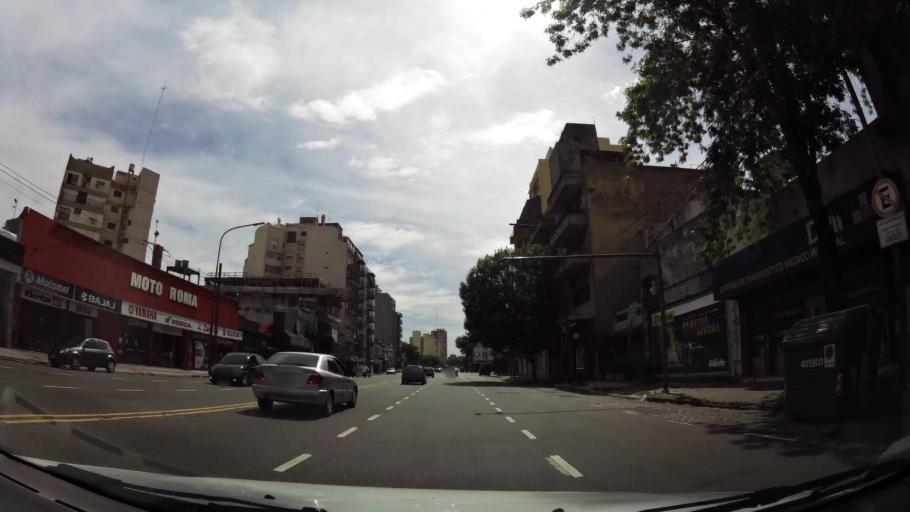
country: AR
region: Buenos Aires F.D.
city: Villa Santa Rita
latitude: -34.6392
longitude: -58.5147
